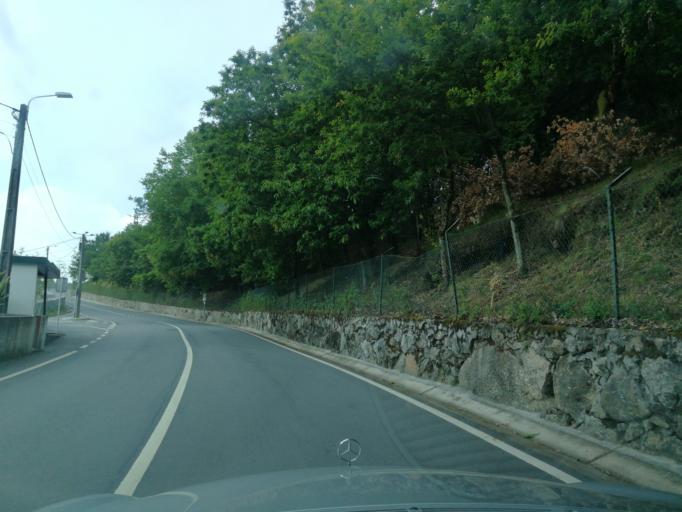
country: PT
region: Braga
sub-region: Braga
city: Braga
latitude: 41.5181
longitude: -8.3712
